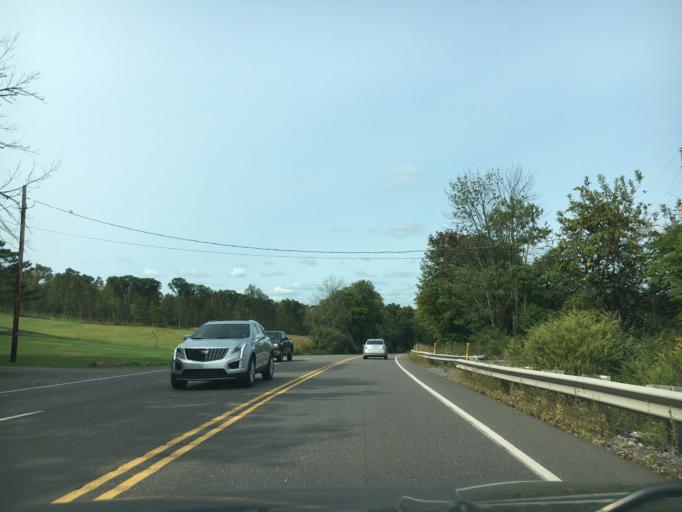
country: US
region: Pennsylvania
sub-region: Carbon County
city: Summit Hill
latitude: 40.7119
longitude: -75.8335
